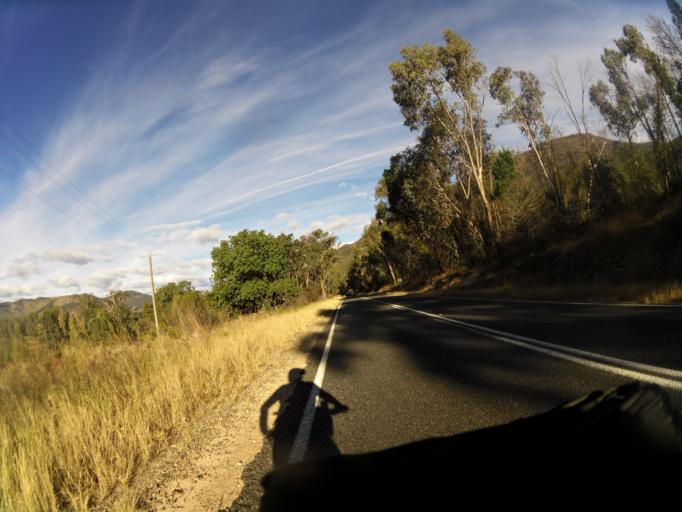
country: AU
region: New South Wales
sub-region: Greater Hume Shire
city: Holbrook
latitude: -35.9883
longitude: 147.8366
